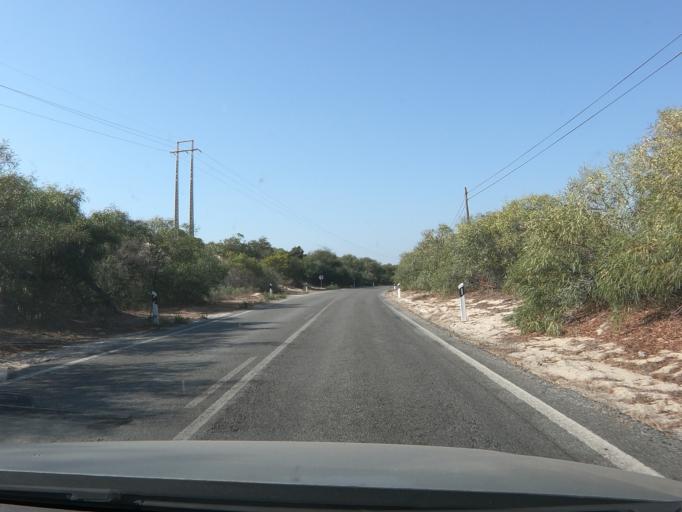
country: PT
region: Setubal
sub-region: Setubal
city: Setubal
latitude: 38.4119
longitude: -8.8140
